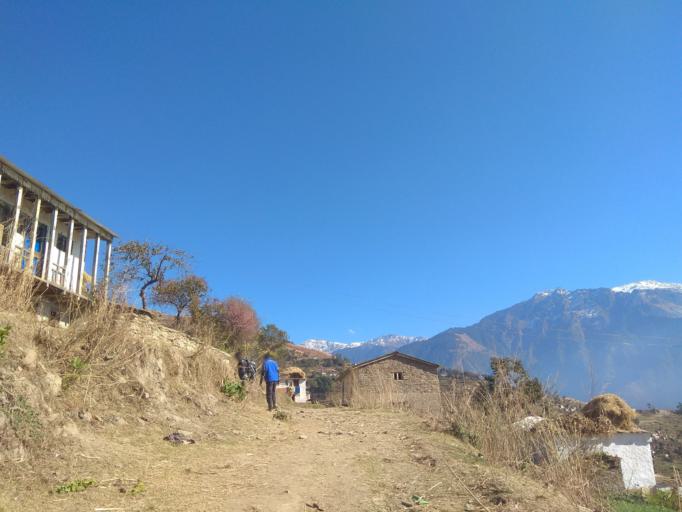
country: NP
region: Far Western
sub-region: Seti Zone
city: Achham
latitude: 29.2558
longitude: 81.6358
